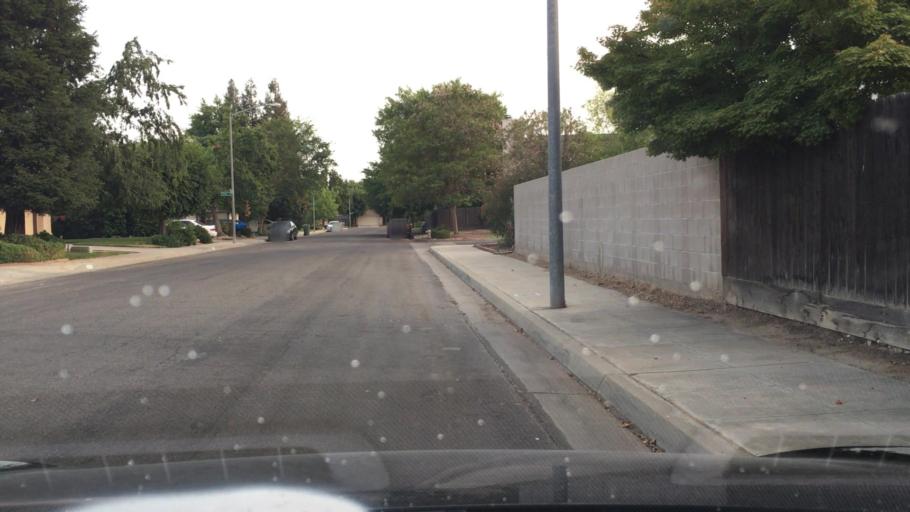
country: US
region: California
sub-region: Fresno County
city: Clovis
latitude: 36.8711
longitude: -119.7433
